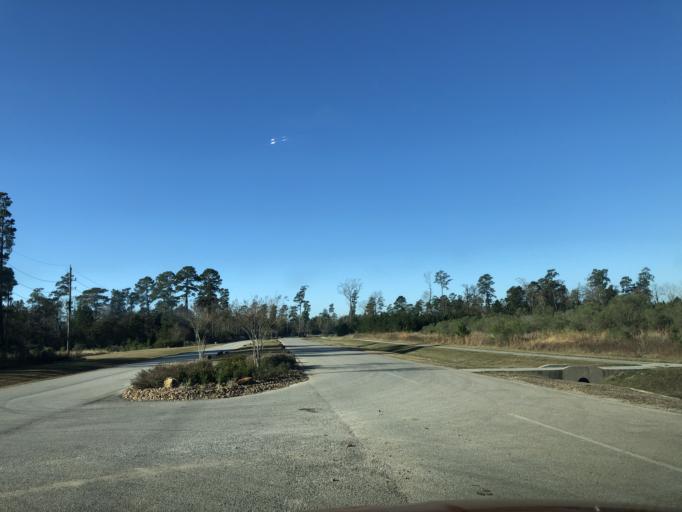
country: US
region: Texas
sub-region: Montgomery County
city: Porter Heights
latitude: 30.0807
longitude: -95.3223
